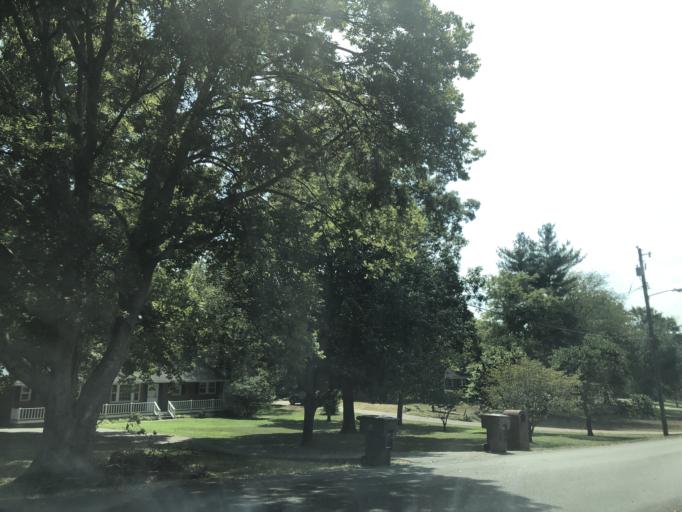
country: US
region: Tennessee
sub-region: Davidson County
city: Lakewood
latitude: 36.1564
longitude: -86.6463
